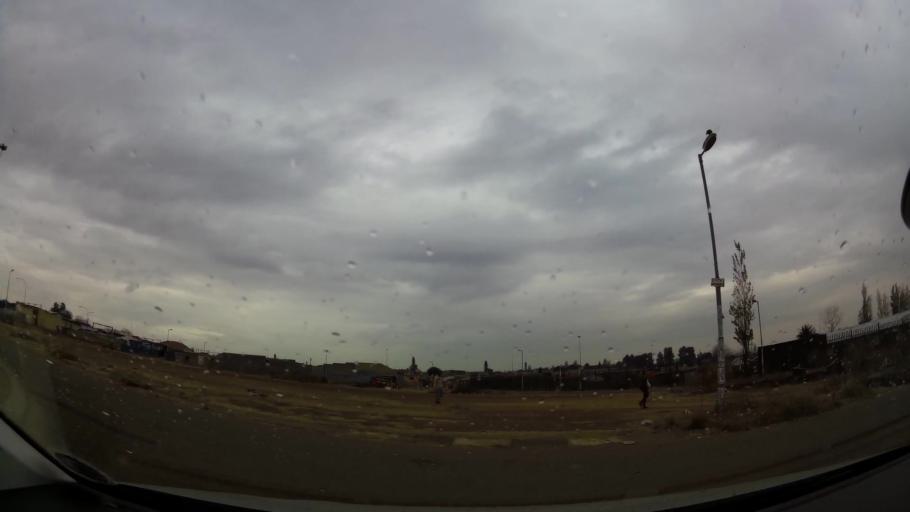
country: ZA
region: Gauteng
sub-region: City of Johannesburg Metropolitan Municipality
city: Soweto
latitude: -26.2519
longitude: 27.8646
